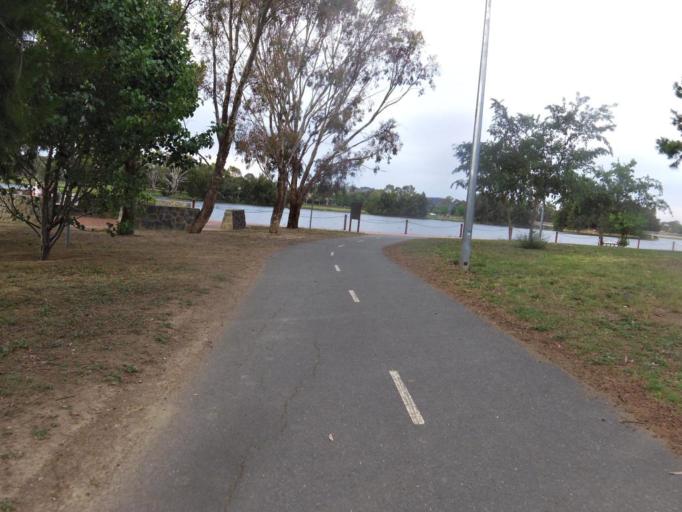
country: AU
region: Australian Capital Territory
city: Kaleen
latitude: -35.1763
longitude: 149.1335
